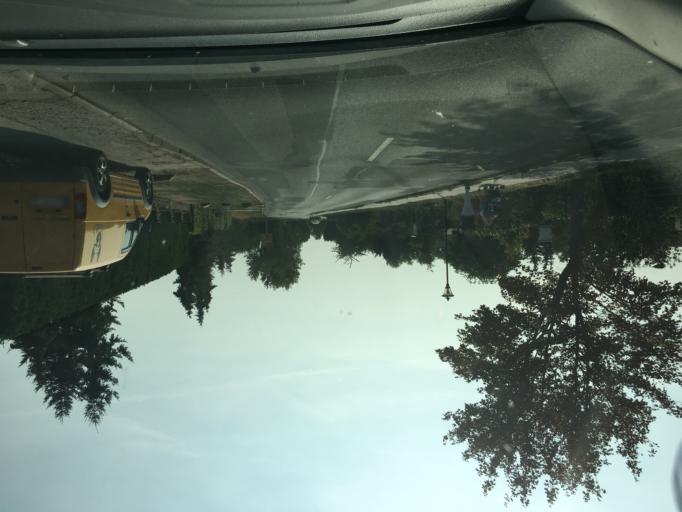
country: DE
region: Saxony-Anhalt
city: Barby
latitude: 51.9705
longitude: 11.8781
